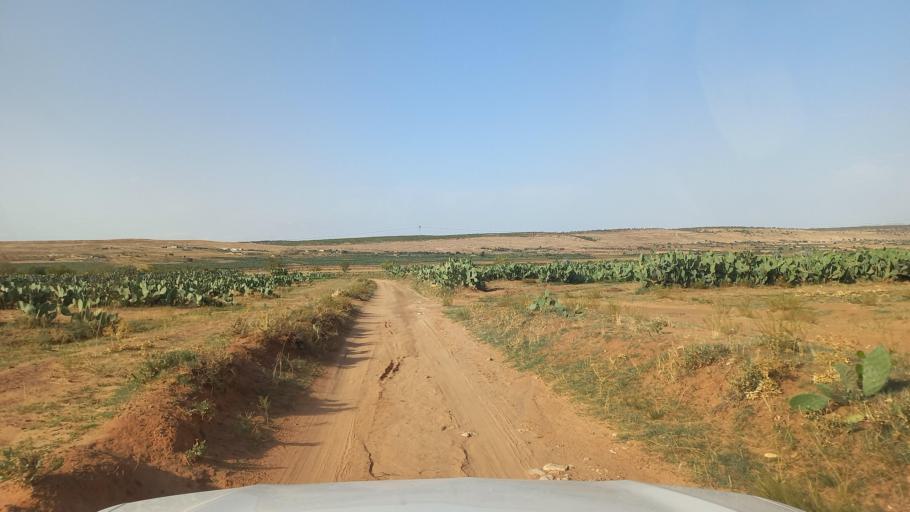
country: TN
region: Al Qasrayn
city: Kasserine
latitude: 35.3492
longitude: 8.8486
